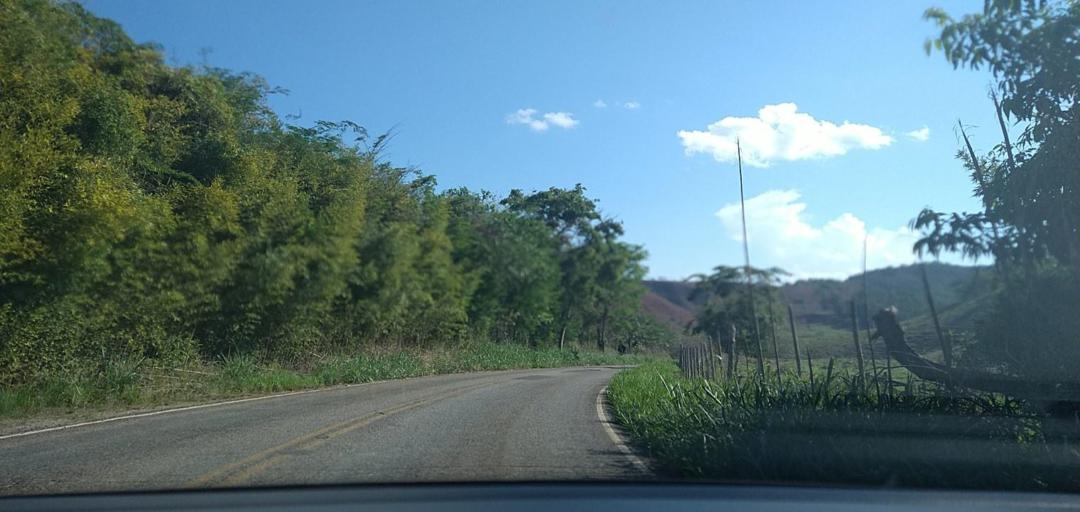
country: BR
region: Minas Gerais
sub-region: Alvinopolis
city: Alvinopolis
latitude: -20.1989
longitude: -42.9275
